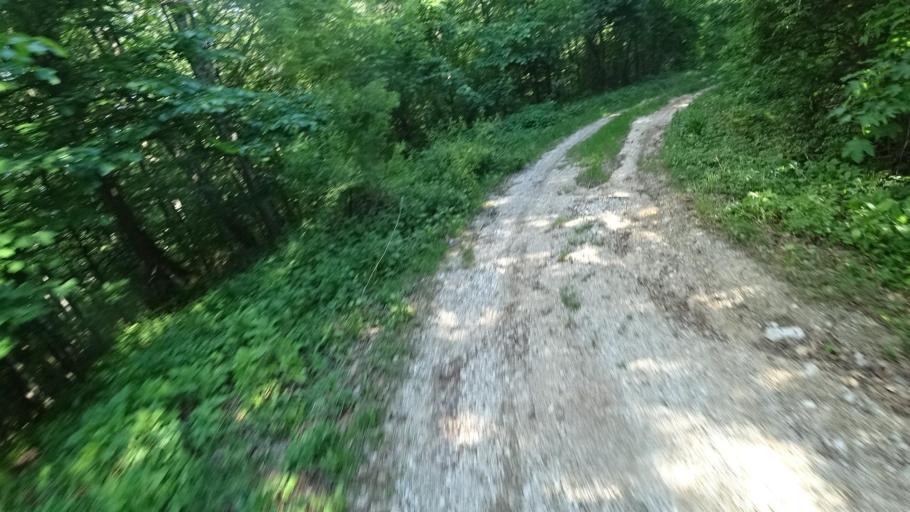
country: BA
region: Federation of Bosnia and Herzegovina
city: Sanica
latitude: 44.6605
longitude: 16.6071
